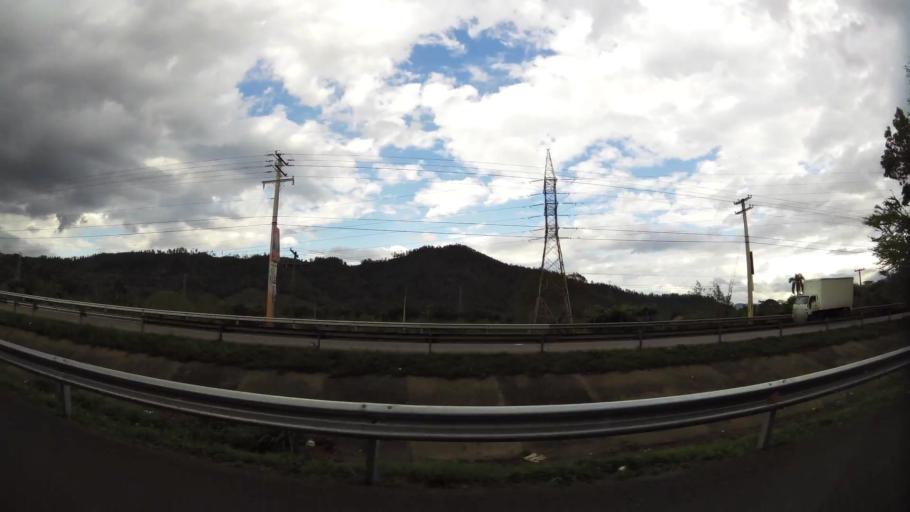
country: DO
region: Monsenor Nouel
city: Bonao
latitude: 18.9647
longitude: -70.4083
